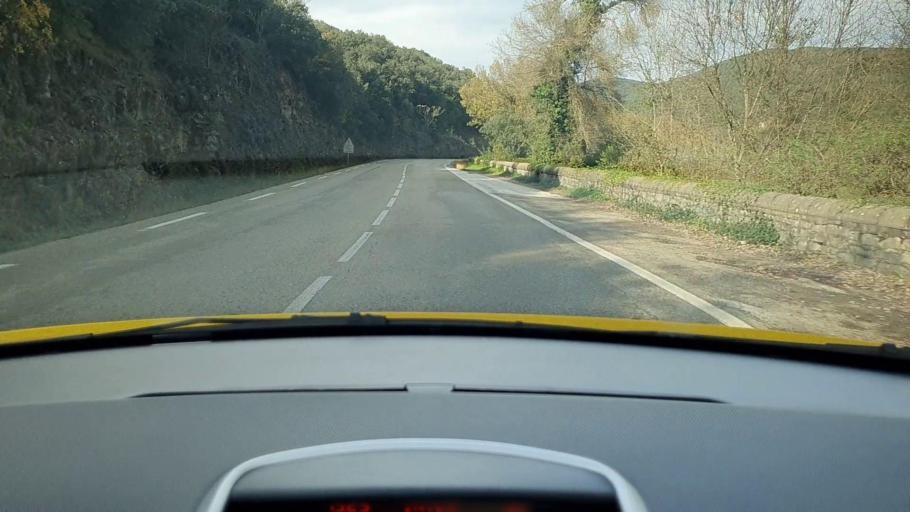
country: FR
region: Languedoc-Roussillon
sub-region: Departement du Gard
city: Anduze
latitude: 44.0682
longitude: 3.9355
